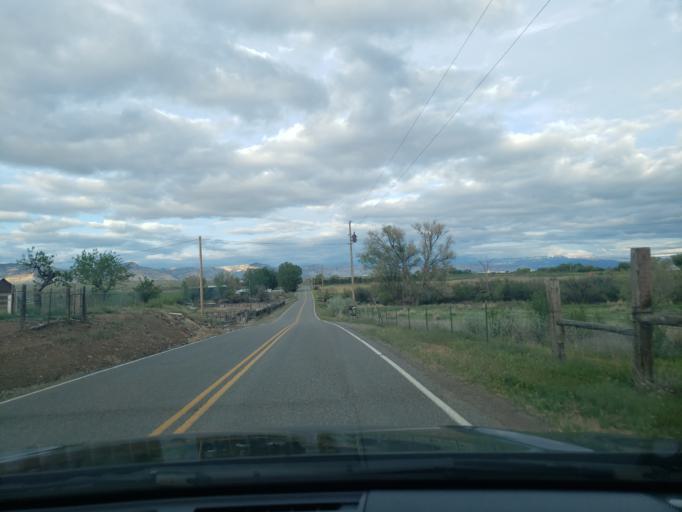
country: US
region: Colorado
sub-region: Mesa County
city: Fruita
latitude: 39.2221
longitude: -108.7078
